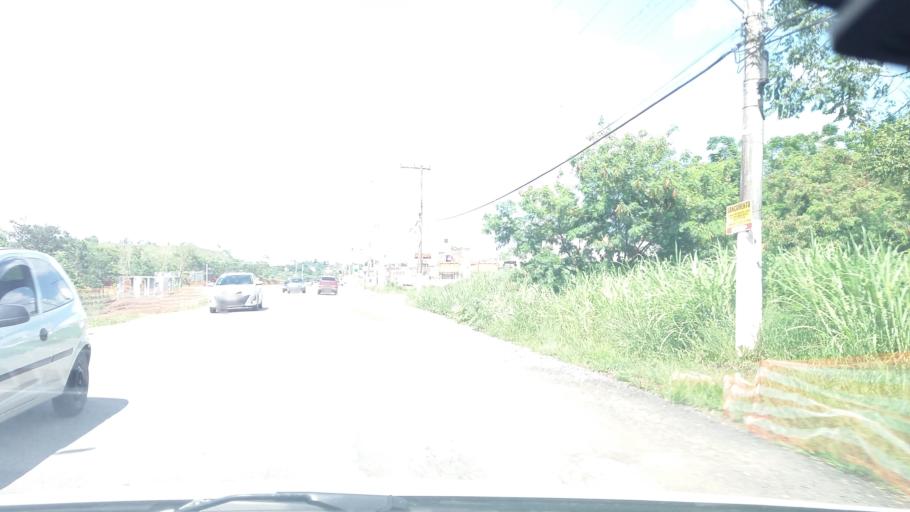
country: BR
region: Sao Paulo
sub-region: Atibaia
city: Atibaia
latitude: -23.1083
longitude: -46.5230
